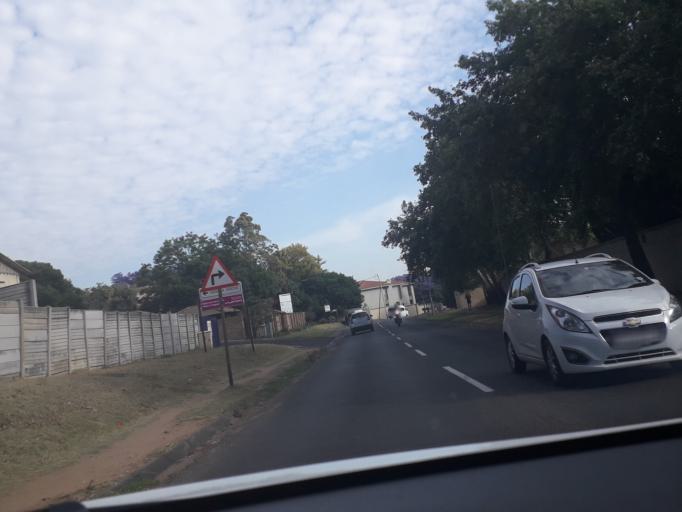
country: ZA
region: Gauteng
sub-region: City of Johannesburg Metropolitan Municipality
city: Diepsloot
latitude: -26.0668
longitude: 28.0007
